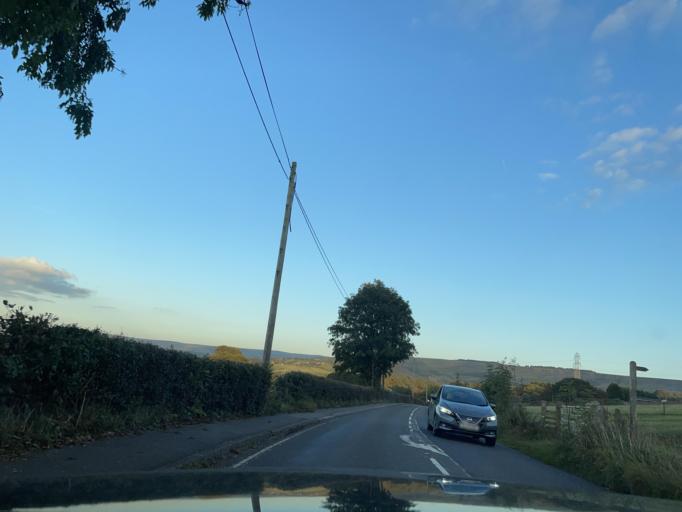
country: GB
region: England
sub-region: Borough of Tameside
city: Longdendale
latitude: 53.4259
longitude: -2.0185
